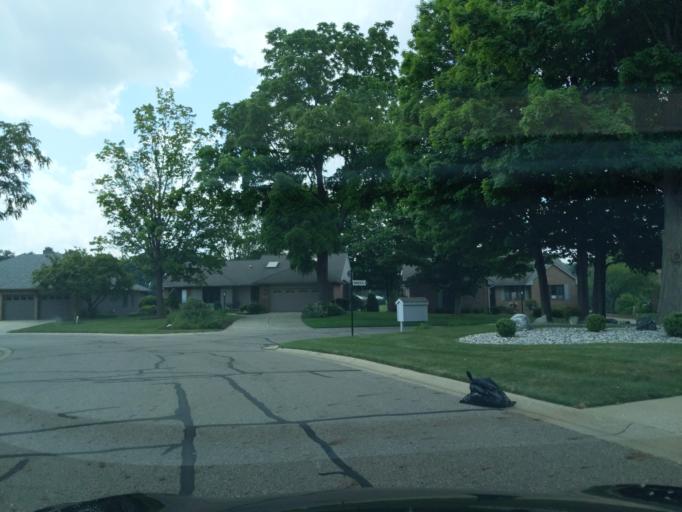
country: US
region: Michigan
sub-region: Eaton County
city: Waverly
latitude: 42.7102
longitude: -84.5985
